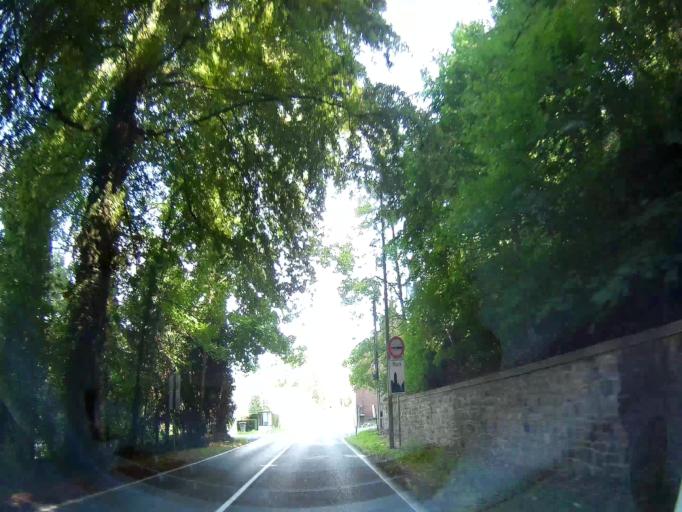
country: BE
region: Wallonia
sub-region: Province de Namur
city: Yvoir
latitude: 50.3370
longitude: 4.8646
